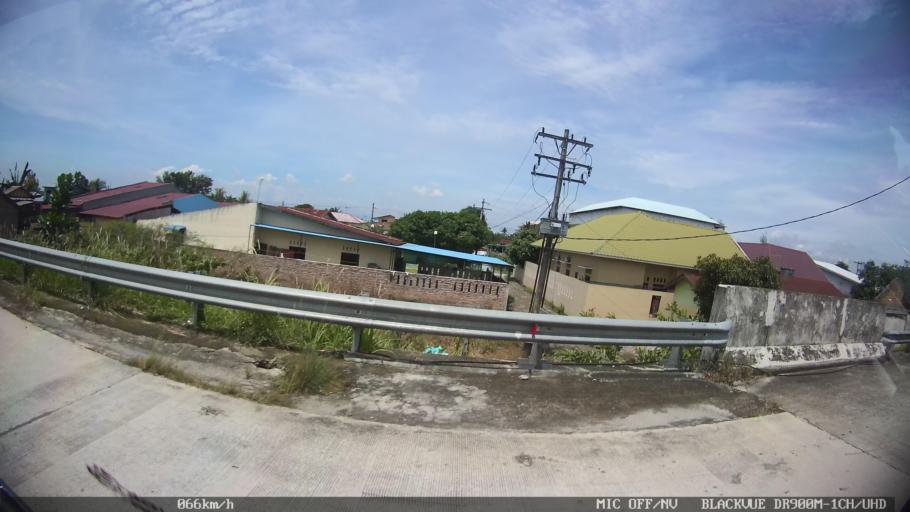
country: ID
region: North Sumatra
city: Perbaungan
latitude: 3.5538
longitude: 98.8877
